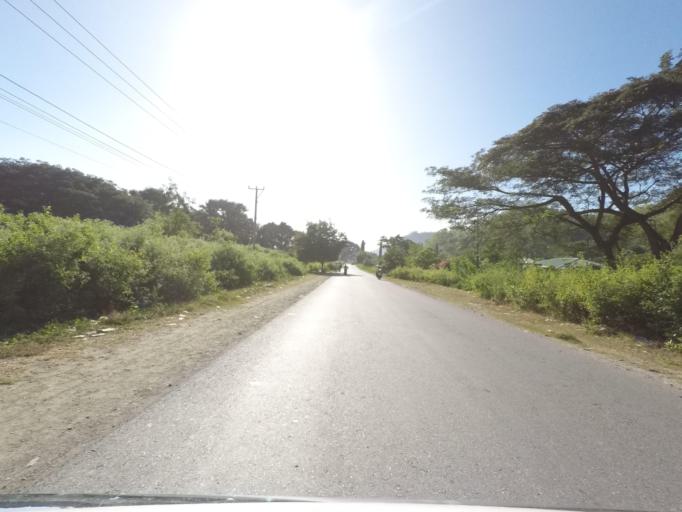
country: TL
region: Dili
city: Dili
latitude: -8.5563
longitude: 125.6512
